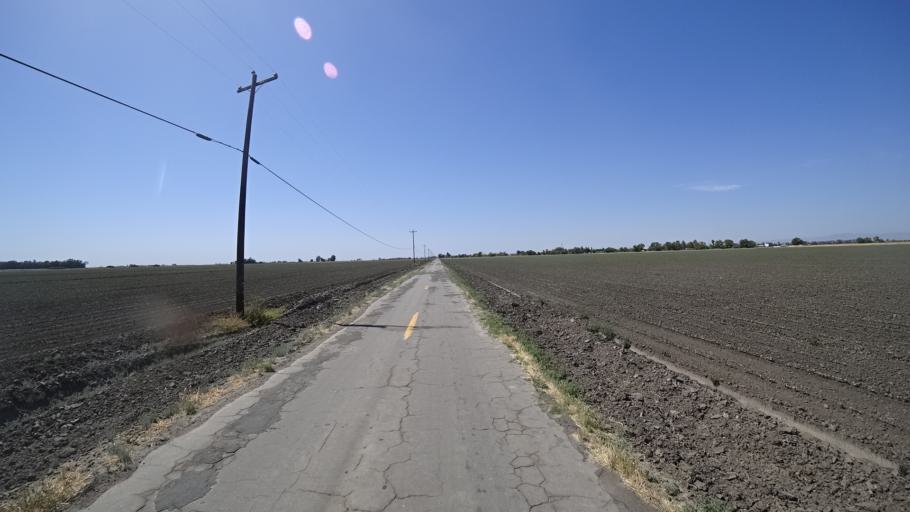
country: US
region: California
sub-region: Kings County
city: Stratford
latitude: 36.2025
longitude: -119.8162
